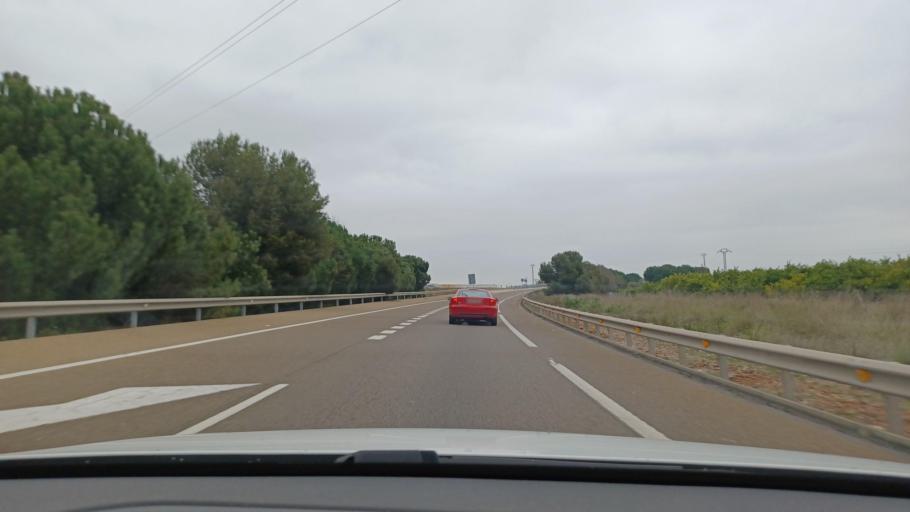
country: ES
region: Valencia
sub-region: Provincia de Castello
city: Nules
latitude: 39.8644
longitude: -0.1647
